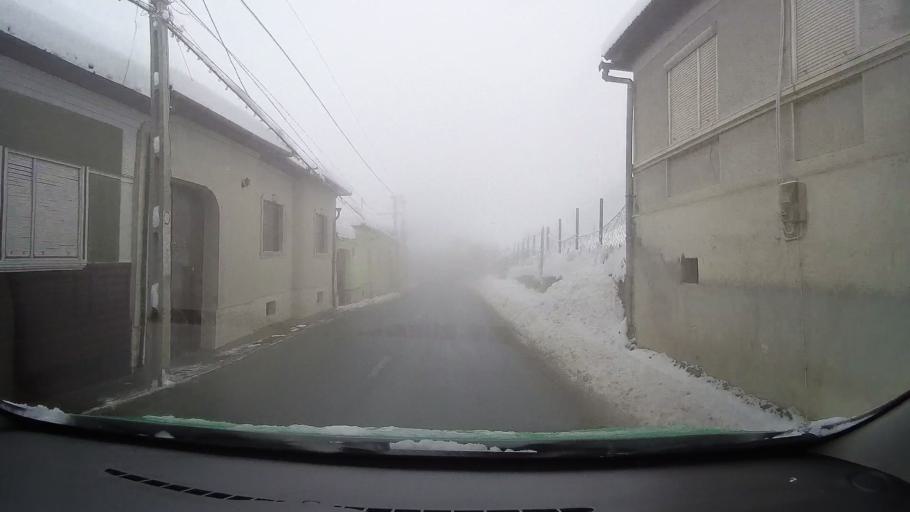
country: RO
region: Sibiu
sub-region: Comuna Poiana Sibiului
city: Poiana Sibiului
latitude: 45.8057
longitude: 23.7240
